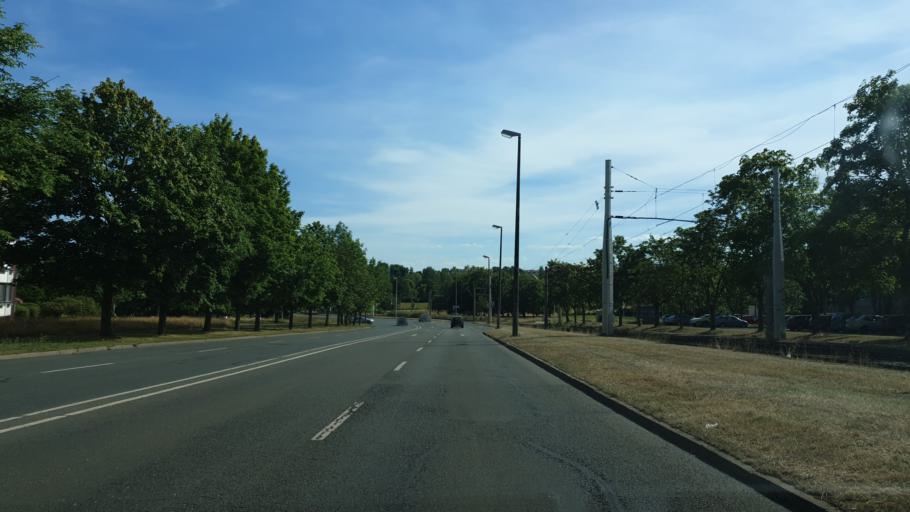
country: DE
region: Thuringia
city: Zedlitz
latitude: 50.8432
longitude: 12.0627
